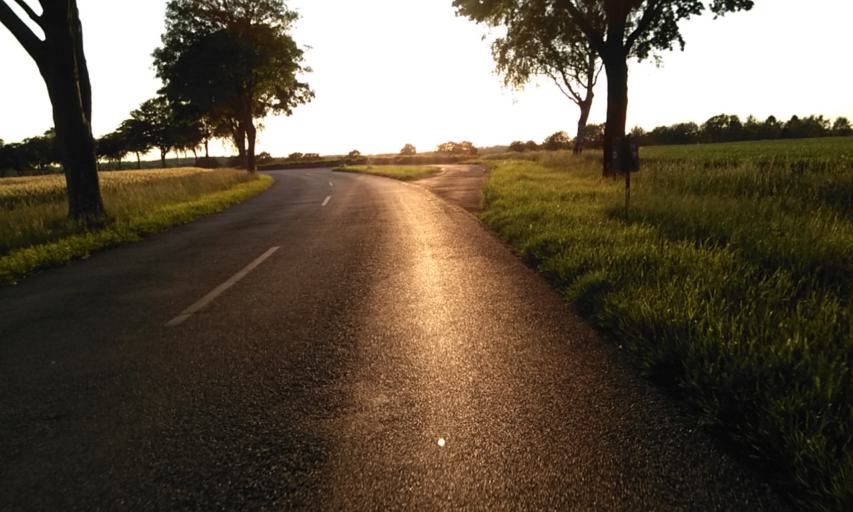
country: DE
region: Lower Saxony
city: Ahlerstedt
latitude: 53.4273
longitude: 9.4458
